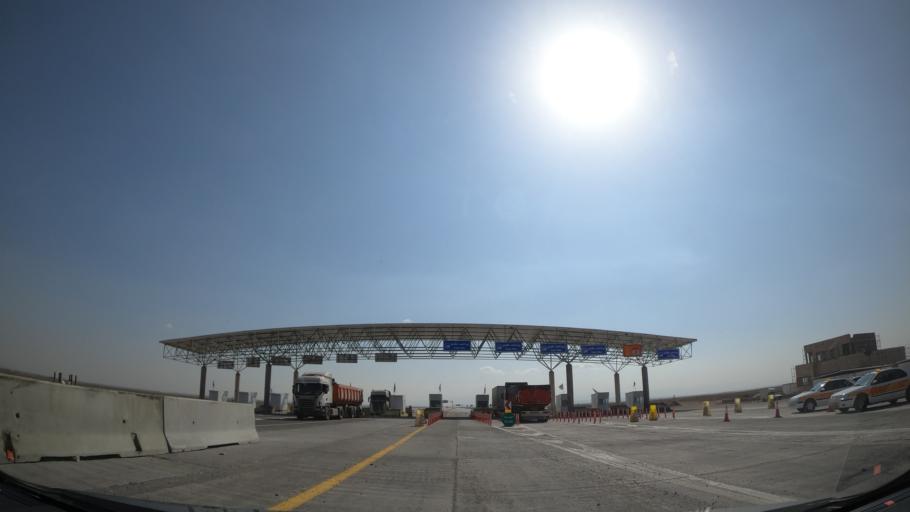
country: IR
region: Qazvin
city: Abyek
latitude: 35.9588
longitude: 50.4645
